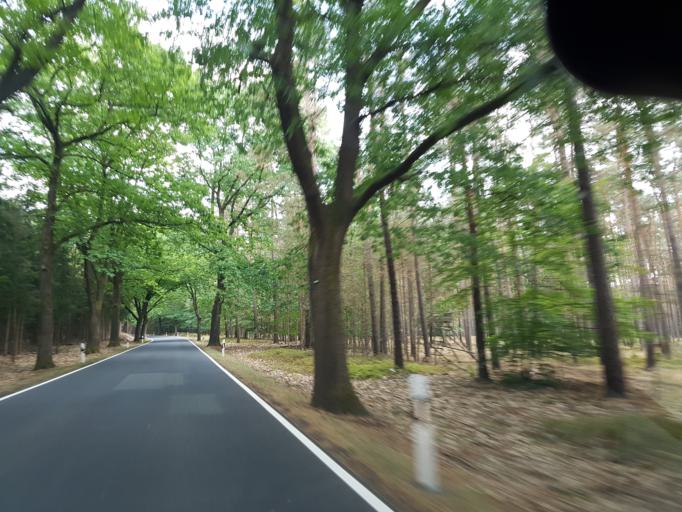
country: DE
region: Brandenburg
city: Wiesenburg
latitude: 52.0580
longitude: 12.4801
